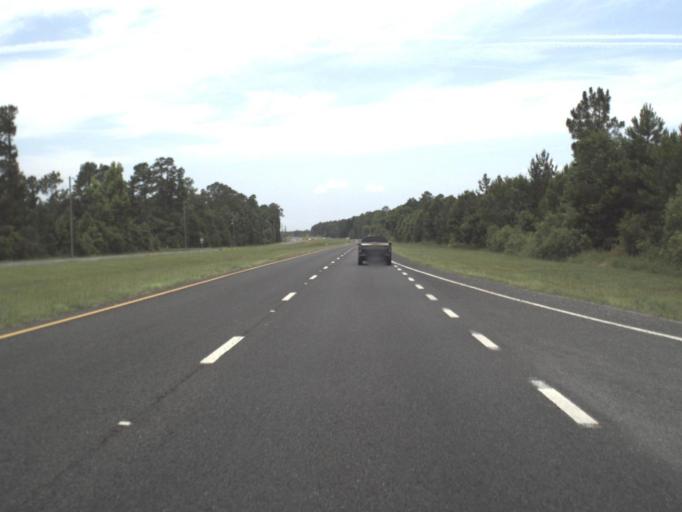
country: US
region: Florida
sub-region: Alachua County
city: Hawthorne
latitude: 29.6002
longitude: -82.1388
